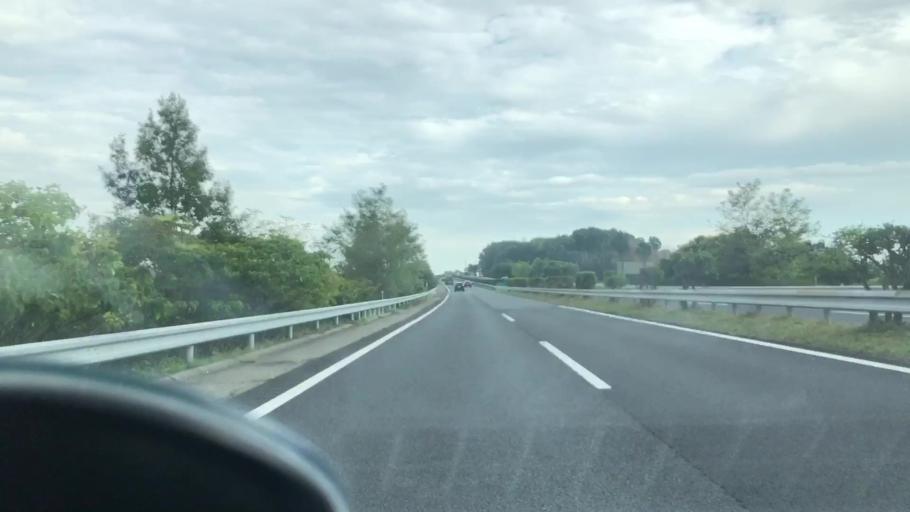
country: JP
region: Hyogo
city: Yashiro
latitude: 34.9356
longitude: 134.8847
